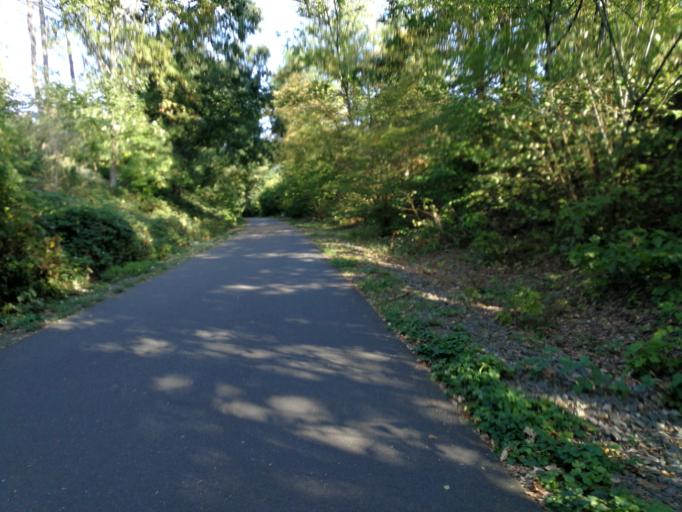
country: DE
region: North Rhine-Westphalia
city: Opladen
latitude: 51.0719
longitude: 7.0209
